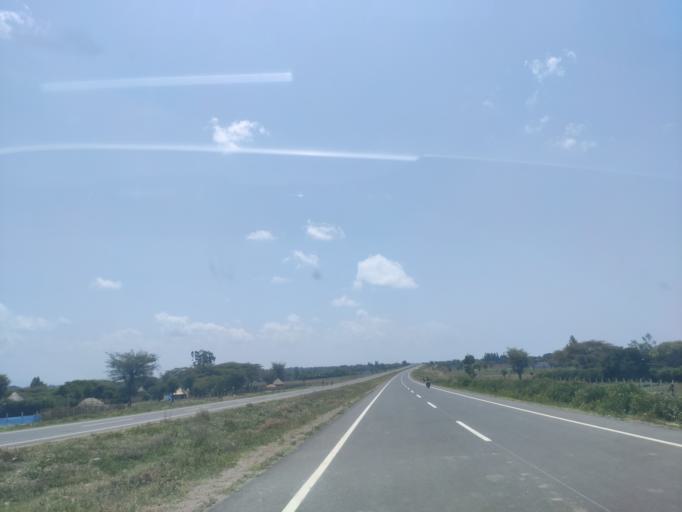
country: ET
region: Oromiya
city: Mojo
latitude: 8.3373
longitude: 38.9686
